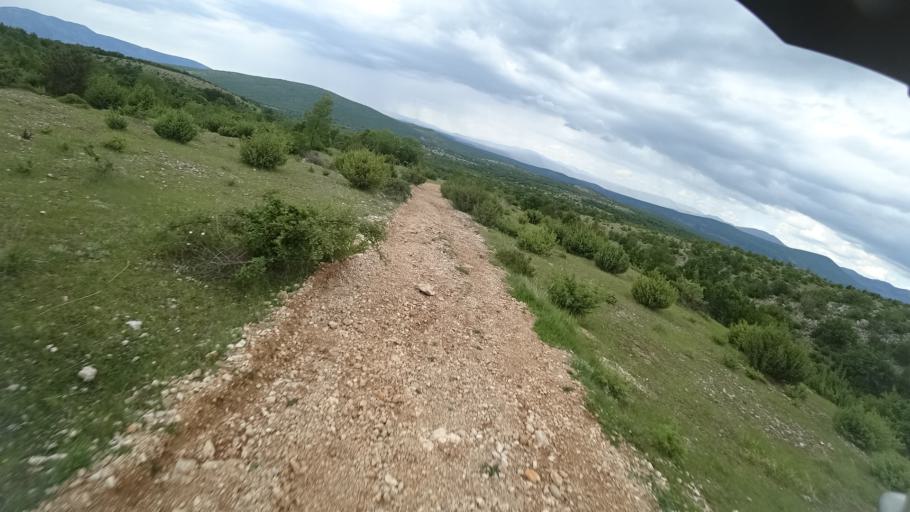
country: HR
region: Sibensko-Kniniska
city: Knin
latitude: 43.9867
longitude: 16.3213
